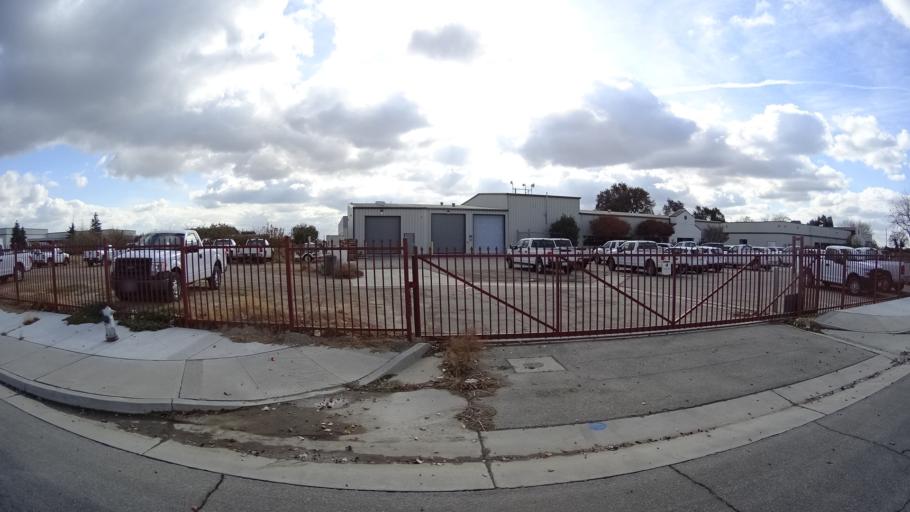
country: US
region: California
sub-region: Kern County
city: Bakersfield
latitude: 35.3466
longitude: -118.9659
